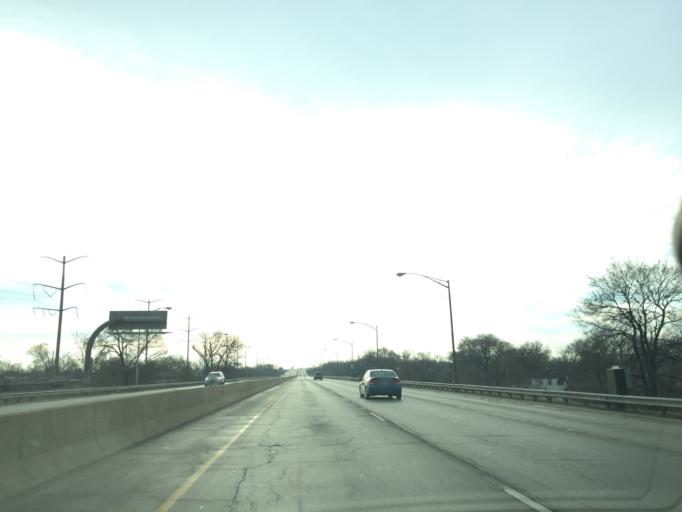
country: US
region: Illinois
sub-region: Cook County
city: Chicago
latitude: 41.7636
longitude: -87.6051
